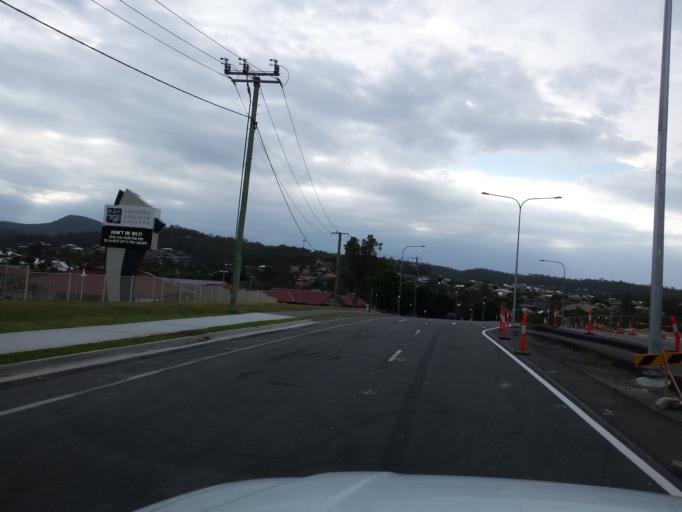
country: AU
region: Queensland
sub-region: Gold Coast
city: Oxenford
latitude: -27.8578
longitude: 153.3064
